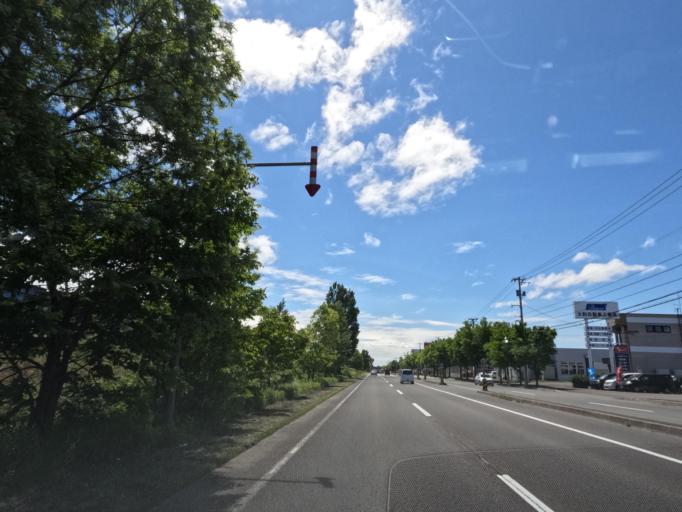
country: JP
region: Hokkaido
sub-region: Asahikawa-shi
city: Asahikawa
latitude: 43.7338
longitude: 142.3639
